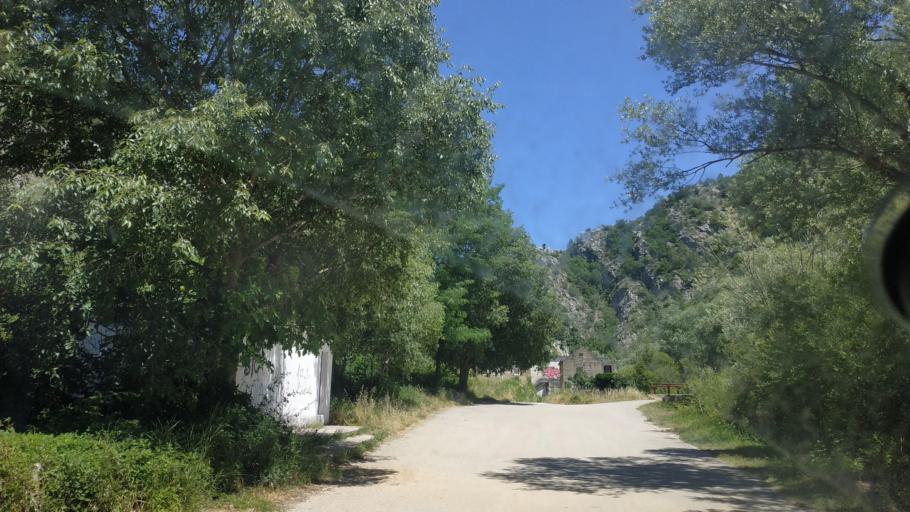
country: HR
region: Sibensko-Kniniska
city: Knin
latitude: 44.0414
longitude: 16.2320
